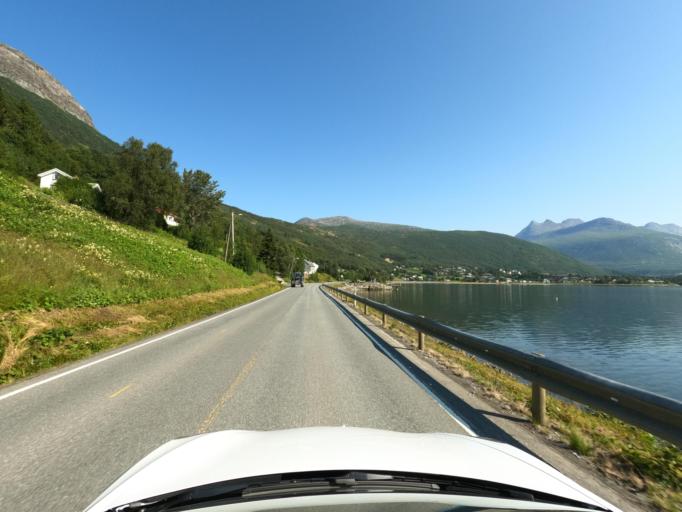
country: NO
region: Nordland
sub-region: Narvik
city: Narvik
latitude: 68.3831
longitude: 17.5828
